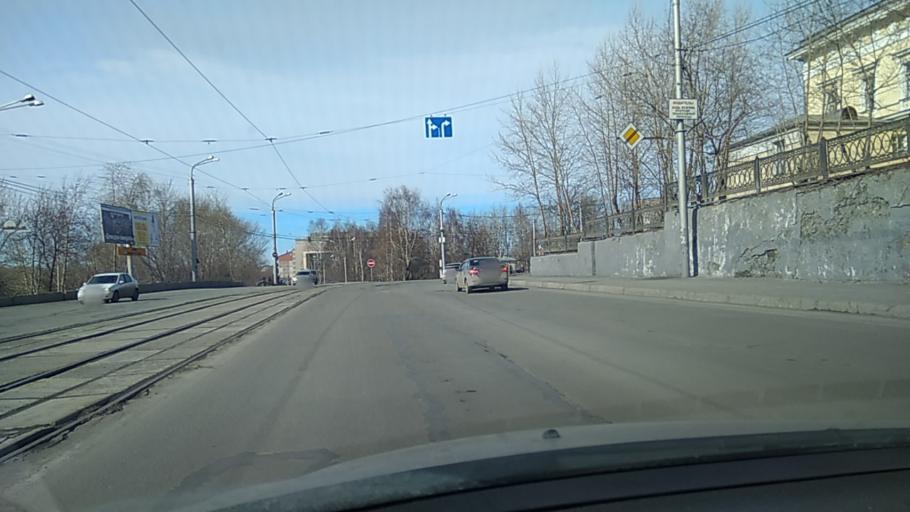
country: RU
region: Sverdlovsk
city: Nizhniy Tagil
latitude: 57.9049
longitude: 59.9501
